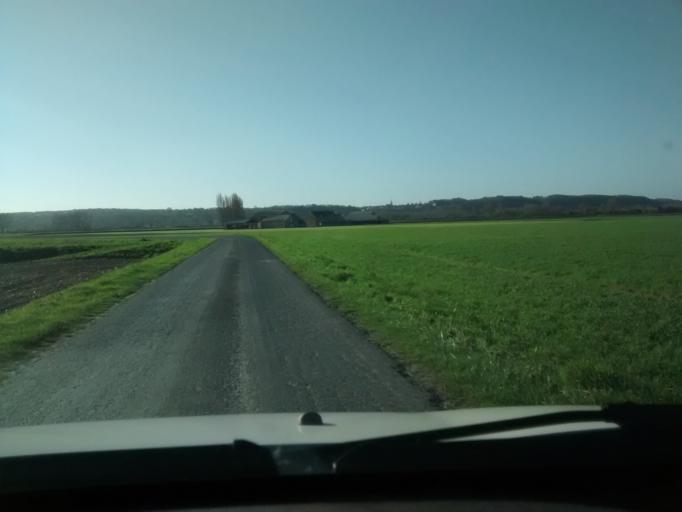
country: FR
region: Brittany
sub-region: Departement d'Ille-et-Vilaine
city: Roz-sur-Couesnon
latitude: 48.6030
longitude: -1.5628
